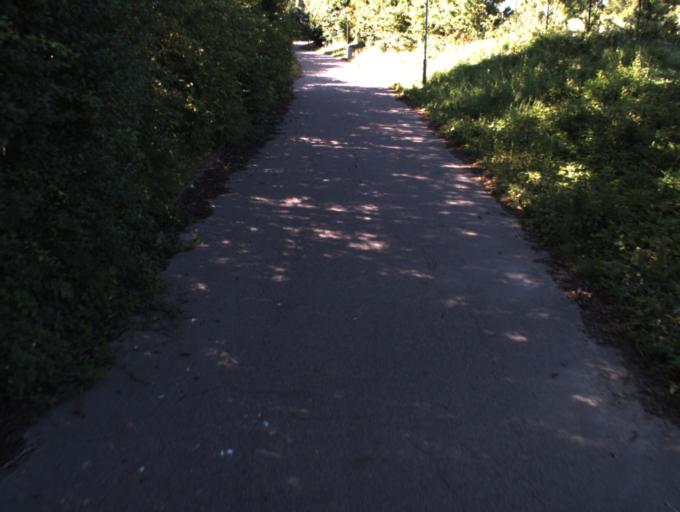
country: SE
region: Skane
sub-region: Helsingborg
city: Gantofta
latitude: 56.0173
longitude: 12.7625
